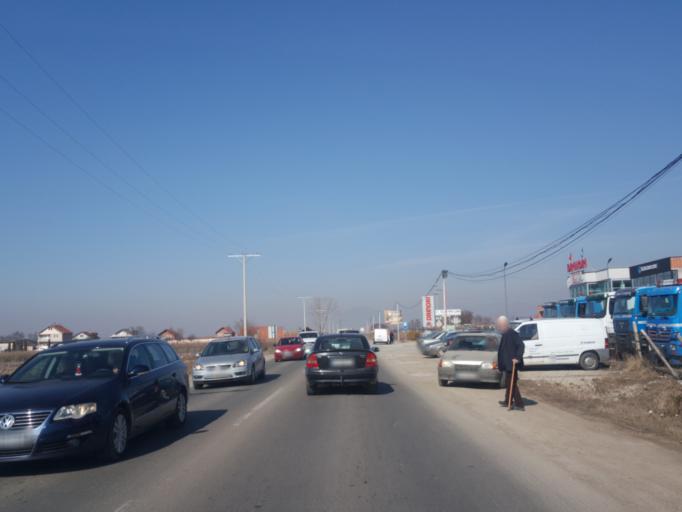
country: XK
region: Mitrovica
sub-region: Vushtrri
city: Vushtrri
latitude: 42.8000
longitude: 20.9958
